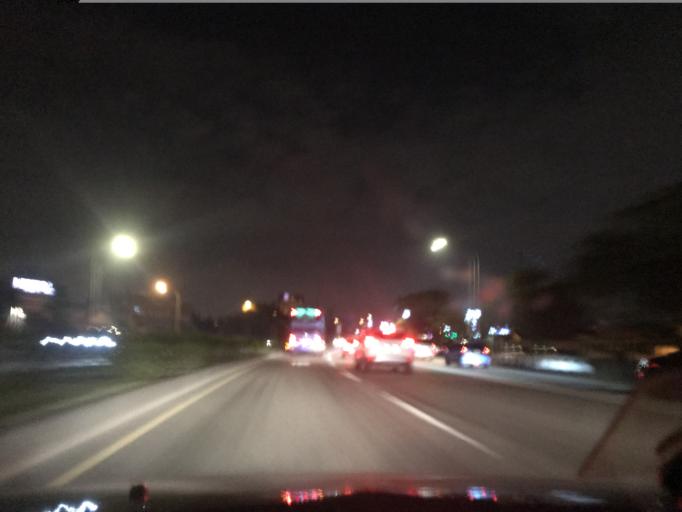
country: TW
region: Taiwan
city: Daxi
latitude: 24.8935
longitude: 121.2626
